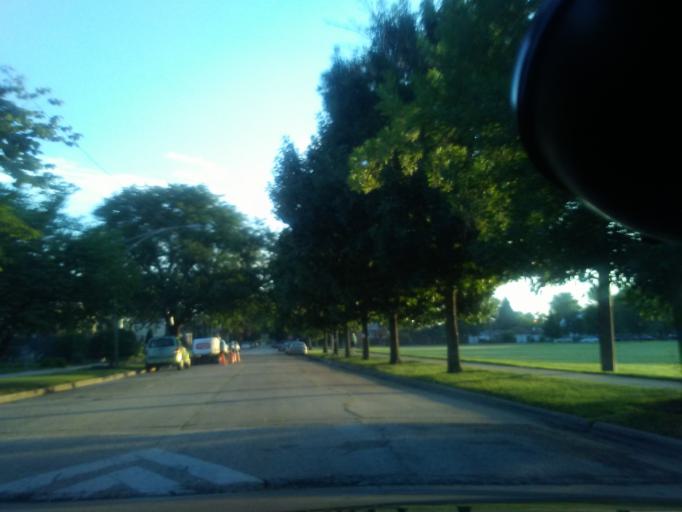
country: US
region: Illinois
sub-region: Cook County
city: Harwood Heights
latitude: 41.9762
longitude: -87.7797
